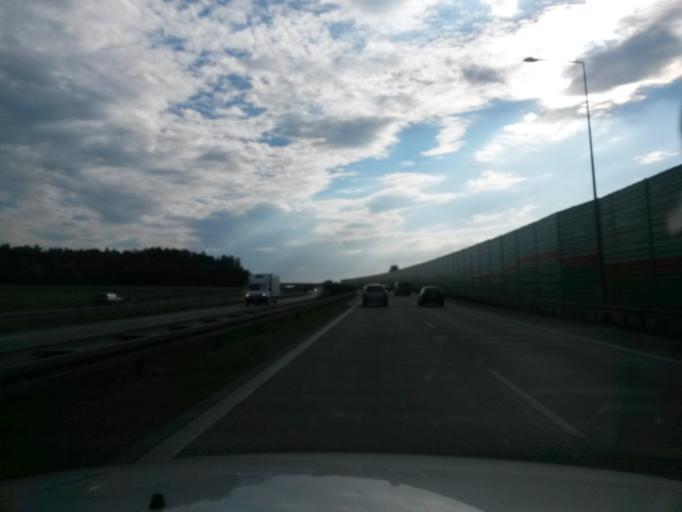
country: PL
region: Lodz Voivodeship
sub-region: Powiat tomaszowski
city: Ujazd
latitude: 51.5223
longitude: 19.9264
